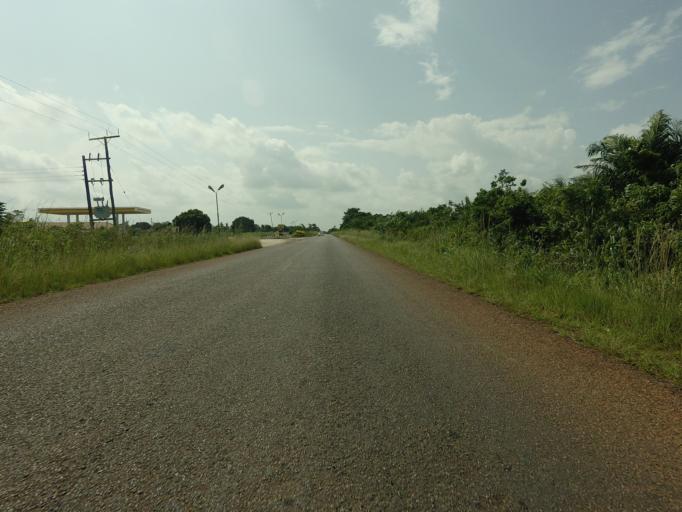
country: TG
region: Maritime
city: Tsevie
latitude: 6.3479
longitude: 0.8718
